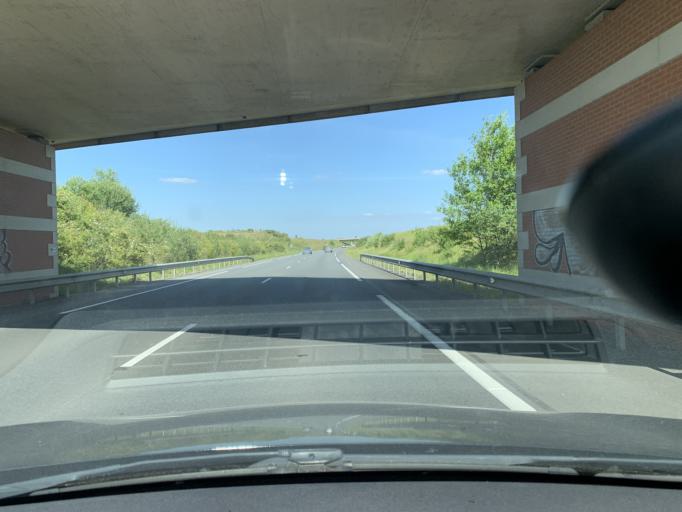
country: FR
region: Nord-Pas-de-Calais
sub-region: Departement du Nord
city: Cambrai
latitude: 50.1494
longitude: 3.2425
